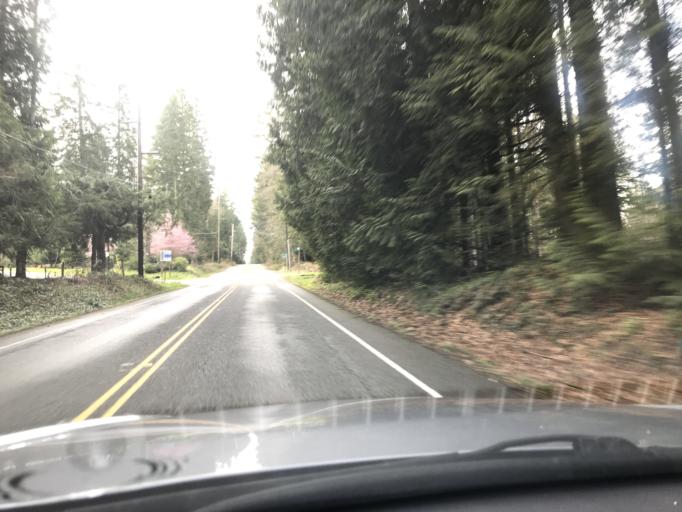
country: US
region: Washington
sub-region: King County
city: Ames Lake
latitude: 47.6510
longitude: -121.9752
